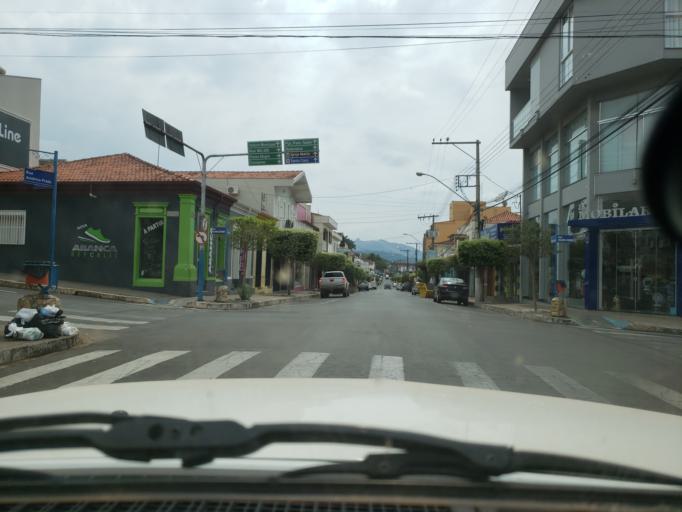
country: BR
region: Minas Gerais
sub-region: Jacutinga
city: Jacutinga
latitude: -22.2891
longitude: -46.6131
